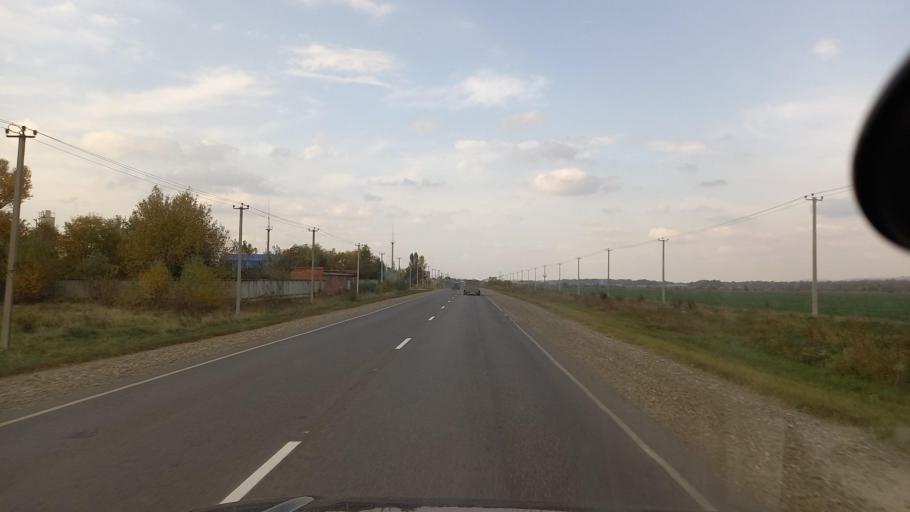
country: RU
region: Krasnodarskiy
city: Mostovskoy
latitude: 44.3787
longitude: 40.8227
